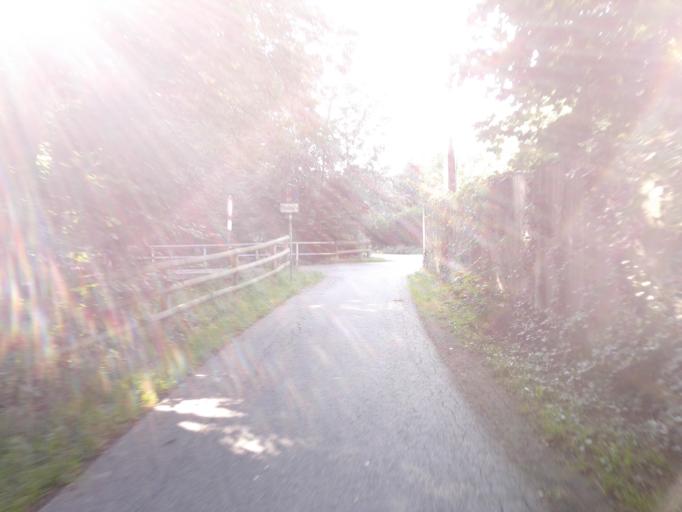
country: AT
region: Styria
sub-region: Graz Stadt
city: Mariatrost
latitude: 47.0766
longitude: 15.4821
